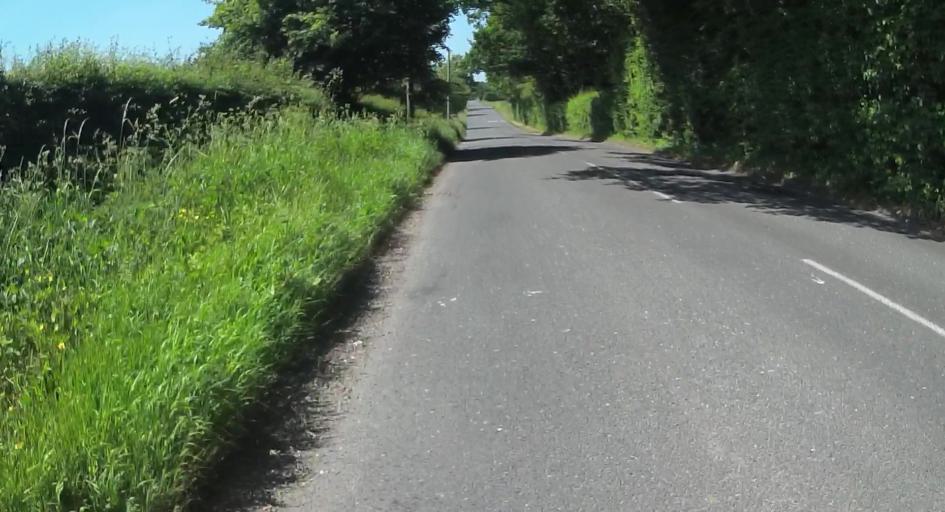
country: GB
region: England
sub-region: Hampshire
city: Kingsclere
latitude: 51.3600
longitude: -1.2245
